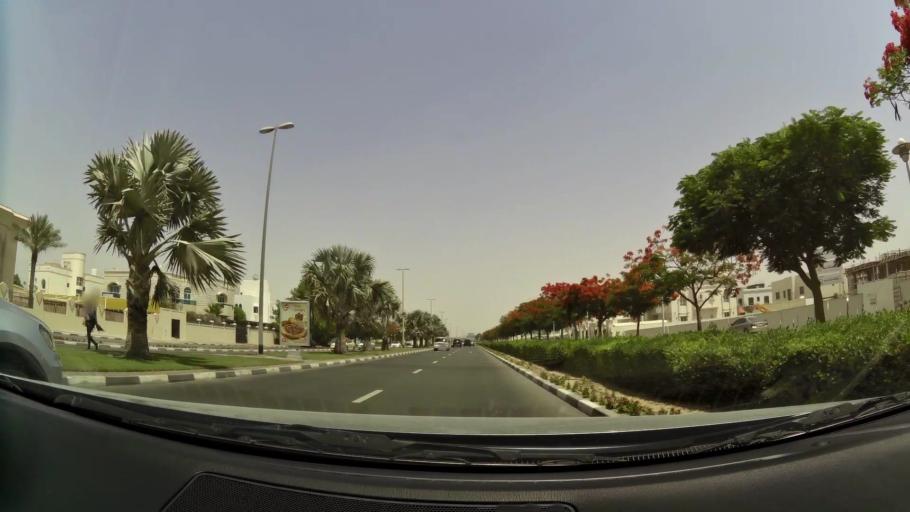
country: AE
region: Dubai
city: Dubai
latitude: 25.1389
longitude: 55.2061
